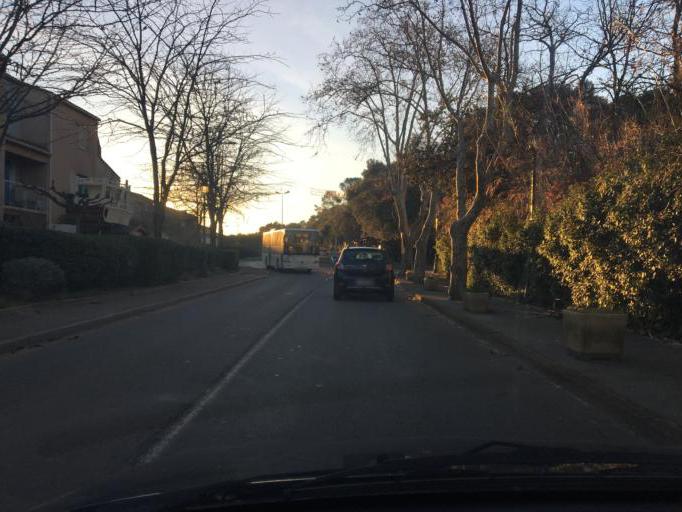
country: FR
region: Provence-Alpes-Cote d'Azur
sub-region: Departement du Var
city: Taradeau
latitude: 43.4525
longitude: 6.4291
